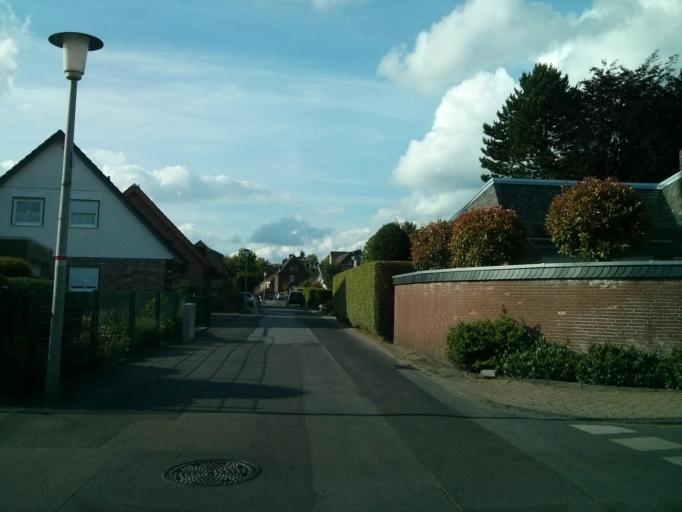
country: DE
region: North Rhine-Westphalia
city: Tonisvorst
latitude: 51.3760
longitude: 6.5040
